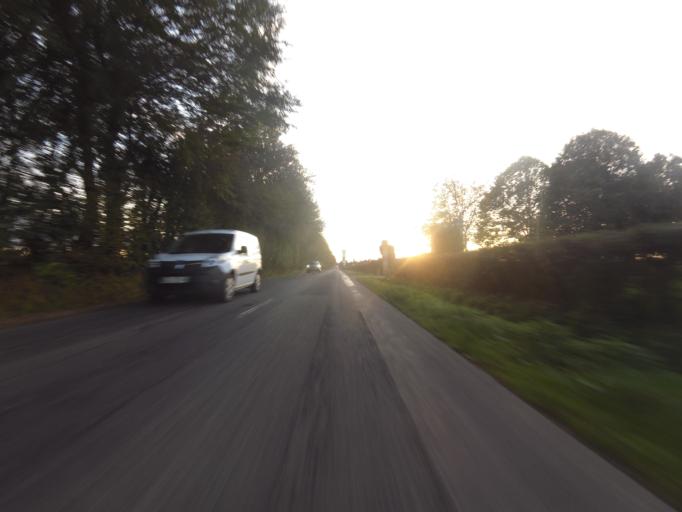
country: FR
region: Lower Normandy
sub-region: Departement du Calvados
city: La Vespiere
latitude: 48.9814
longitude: 0.3483
